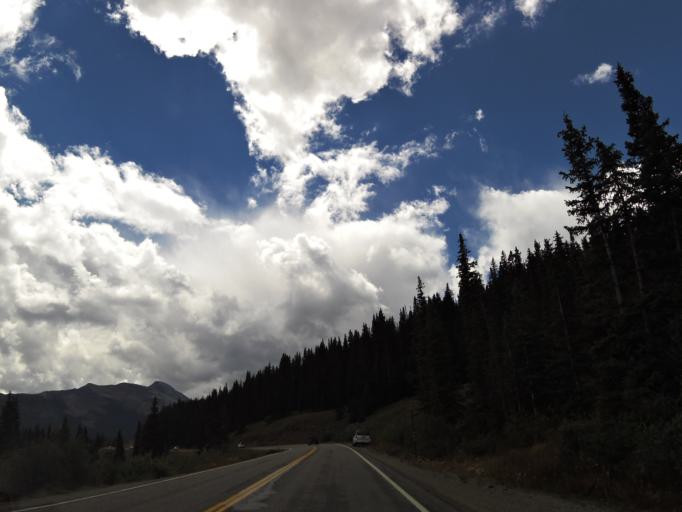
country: US
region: Colorado
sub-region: San Juan County
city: Silverton
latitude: 37.7628
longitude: -107.6802
